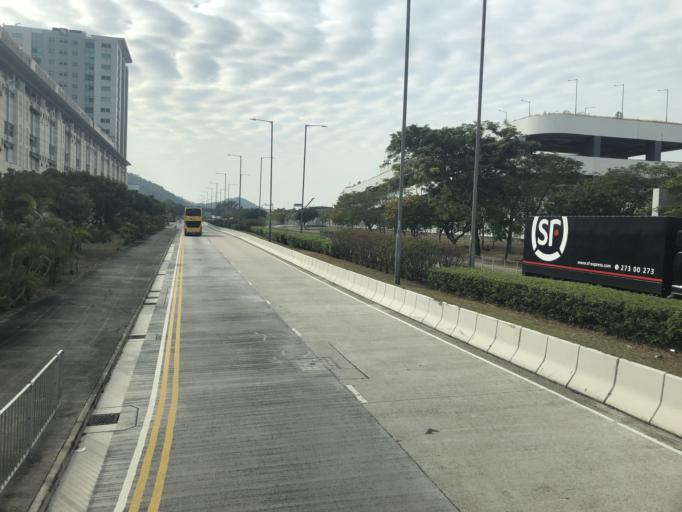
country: HK
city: Tai O
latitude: 22.2958
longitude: 113.9265
